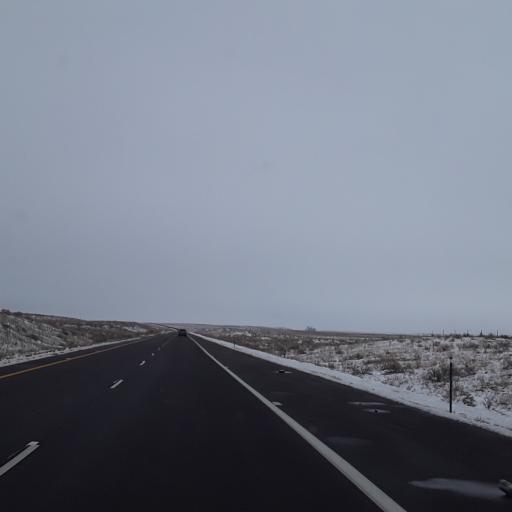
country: US
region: Colorado
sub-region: Logan County
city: Sterling
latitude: 40.6282
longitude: -103.1647
